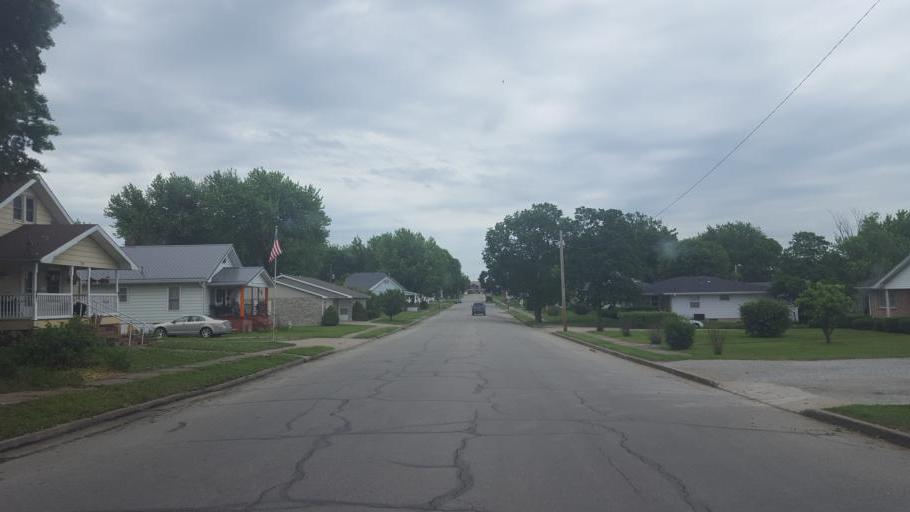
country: US
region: Missouri
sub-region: Moniteau County
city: California
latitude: 38.6288
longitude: -92.5722
